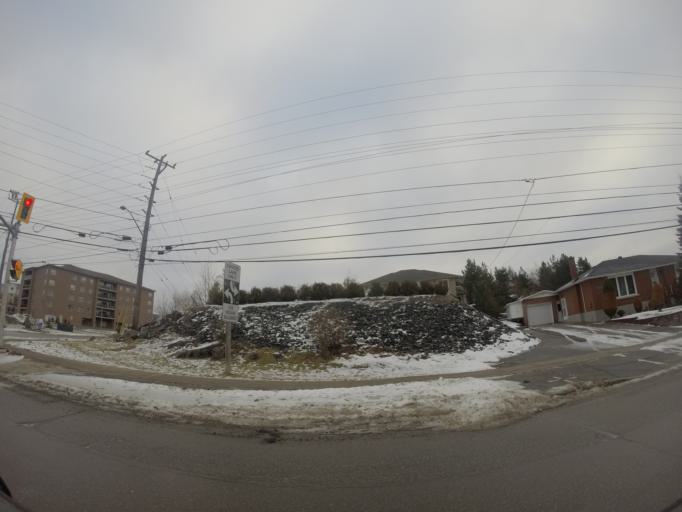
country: CA
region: Ontario
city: Greater Sudbury
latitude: 46.4643
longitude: -81.0282
